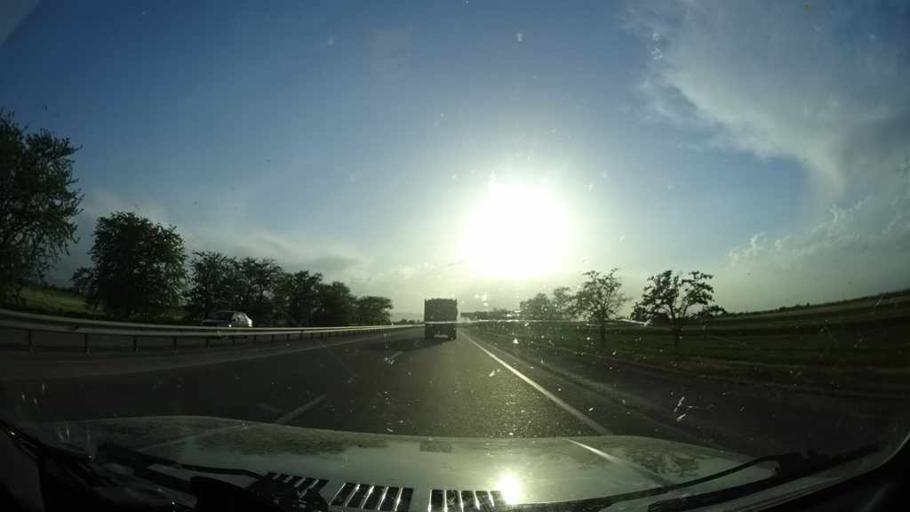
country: AZ
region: Samux
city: Samux
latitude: 40.6896
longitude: 46.5256
